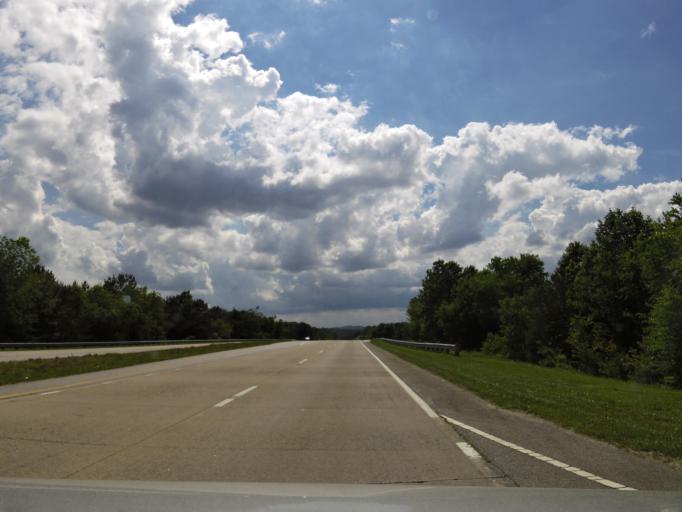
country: US
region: Georgia
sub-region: Union County
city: Blairsville
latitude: 34.8696
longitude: -83.9737
